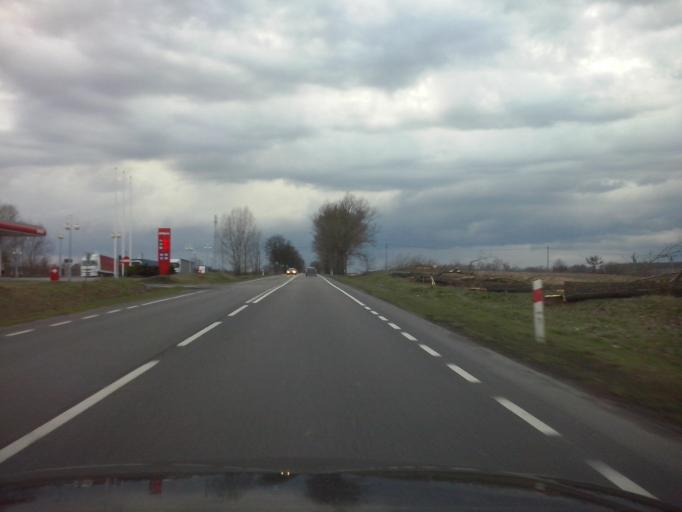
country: PL
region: Lublin Voivodeship
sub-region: Powiat chelmski
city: Rejowiec
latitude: 51.1686
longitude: 23.3403
